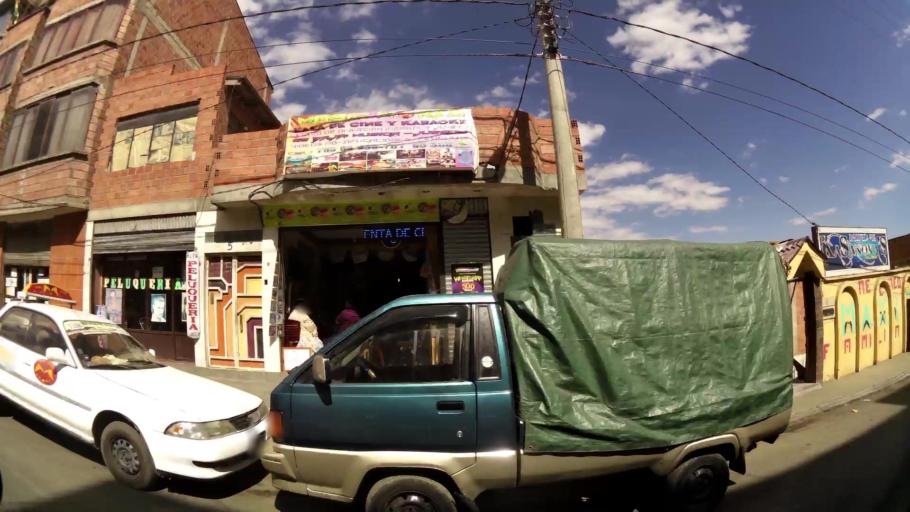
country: BO
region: La Paz
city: La Paz
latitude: -16.4610
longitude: -68.1045
